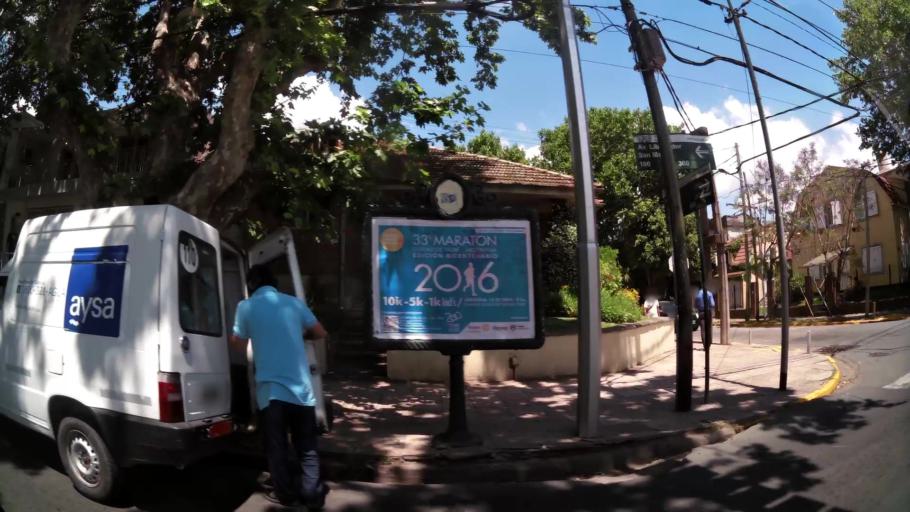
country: AR
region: Buenos Aires
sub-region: Partido de Tigre
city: Tigre
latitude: -34.4206
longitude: -58.5843
